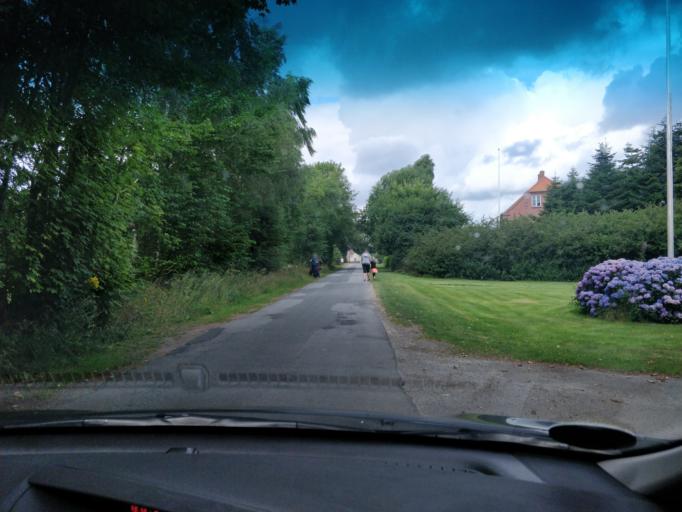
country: DK
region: South Denmark
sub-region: Assens Kommune
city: Assens
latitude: 55.2571
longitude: 9.7405
